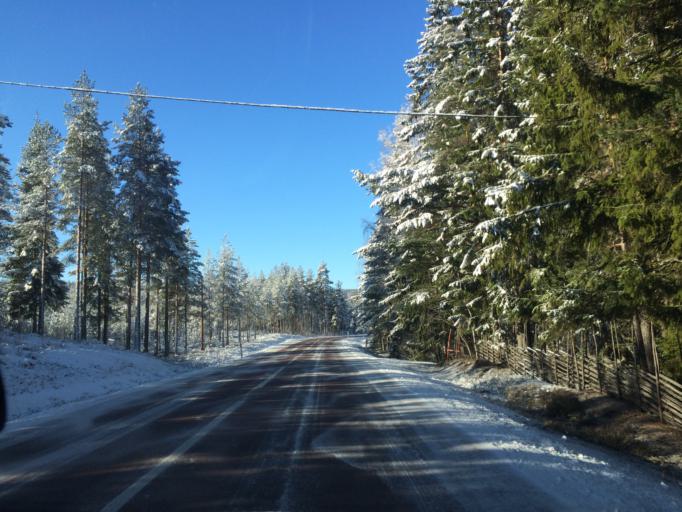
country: SE
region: Dalarna
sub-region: Mora Kommun
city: Mora
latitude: 60.8623
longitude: 14.3436
